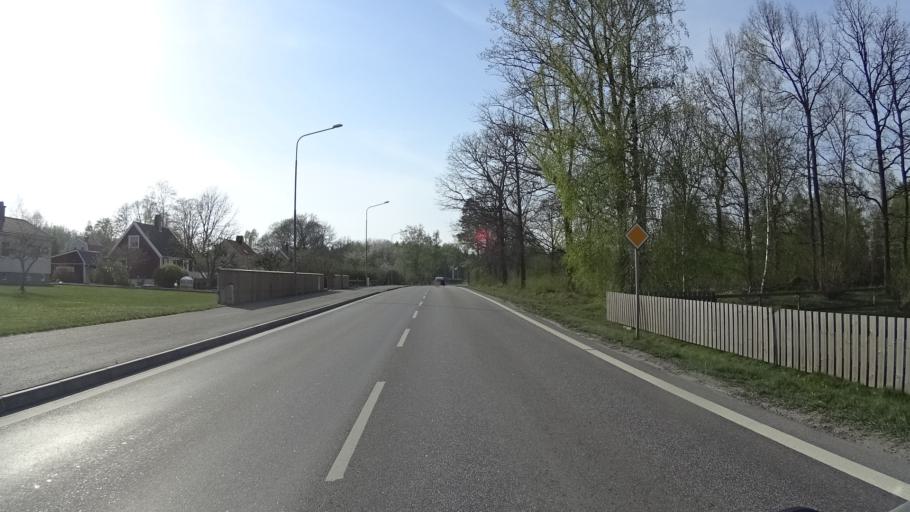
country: SE
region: Vaestra Goetaland
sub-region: Gotene Kommun
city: Goetene
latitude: 58.6304
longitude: 13.4436
